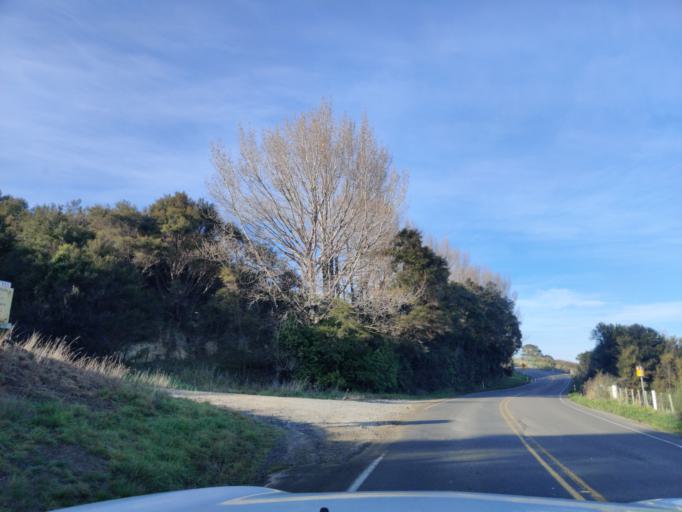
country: NZ
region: Manawatu-Wanganui
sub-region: Palmerston North City
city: Palmerston North
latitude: -40.2836
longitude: 175.7718
